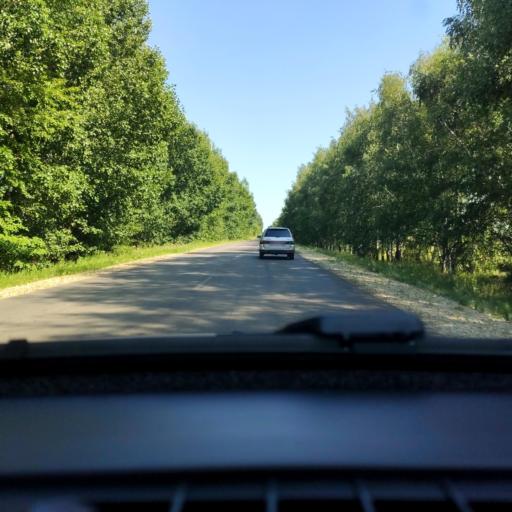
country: RU
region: Voronezj
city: Pereleshinskiy
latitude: 51.6409
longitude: 40.3065
